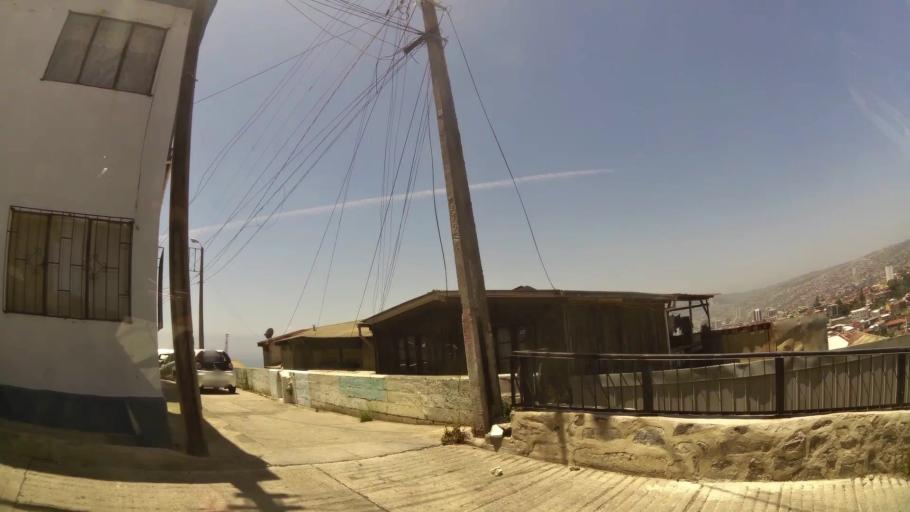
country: CL
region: Valparaiso
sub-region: Provincia de Valparaiso
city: Valparaiso
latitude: -33.0355
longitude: -71.6353
